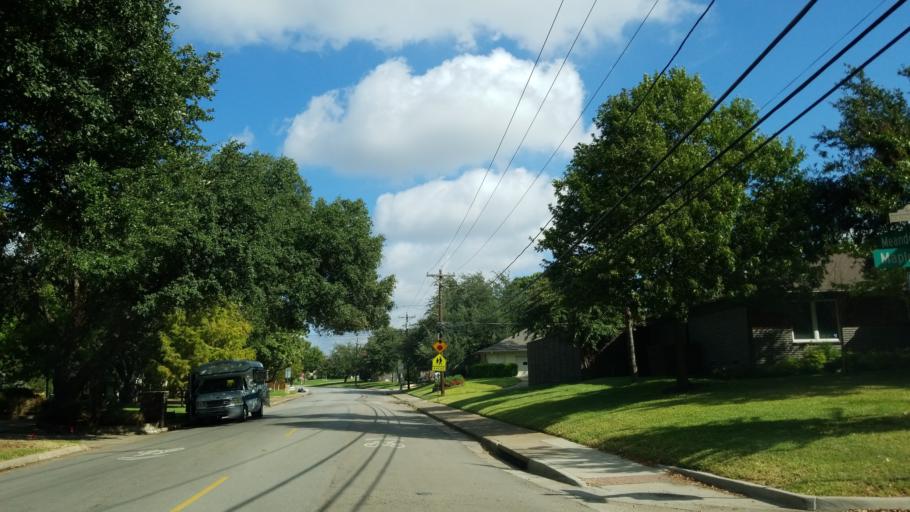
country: US
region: Texas
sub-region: Dallas County
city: Richardson
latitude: 32.9442
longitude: -96.7780
